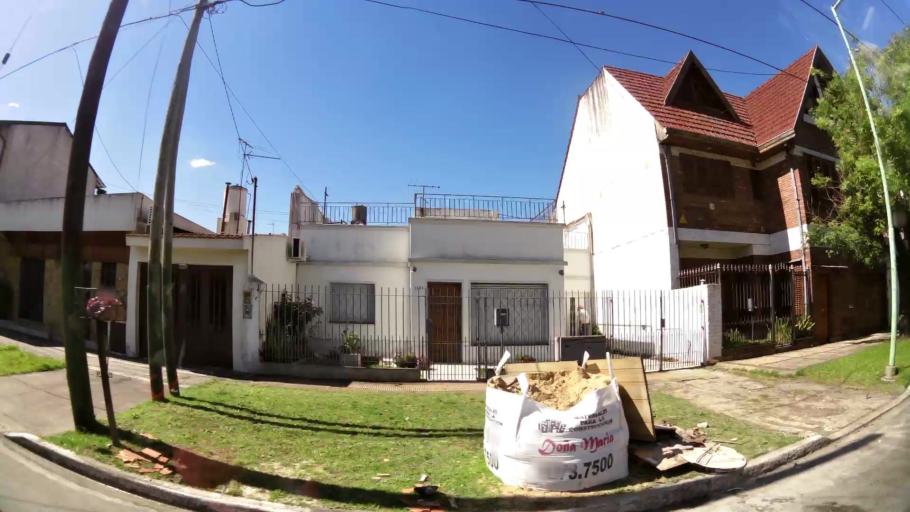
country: AR
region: Buenos Aires
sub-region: Partido de Lomas de Zamora
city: Lomas de Zamora
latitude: -34.7397
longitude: -58.4163
